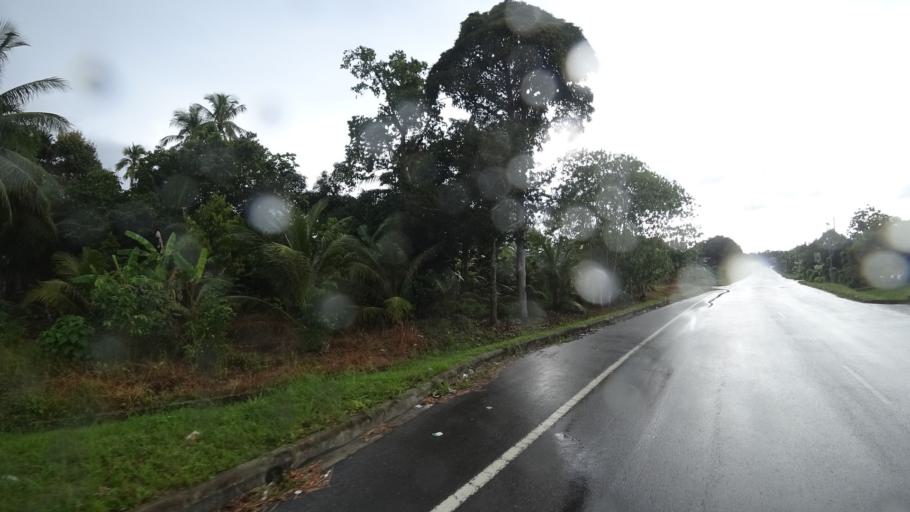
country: BN
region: Brunei and Muara
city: Bandar Seri Begawan
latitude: 4.8347
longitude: 114.9161
